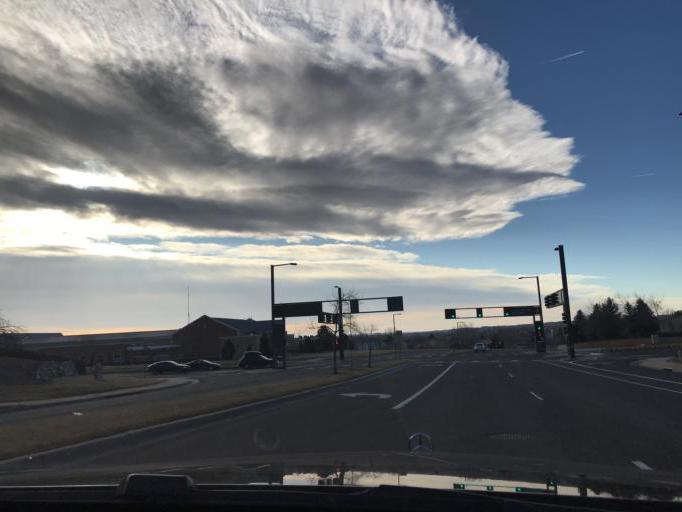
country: US
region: Colorado
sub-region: Boulder County
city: Superior
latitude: 39.9731
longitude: -105.1651
